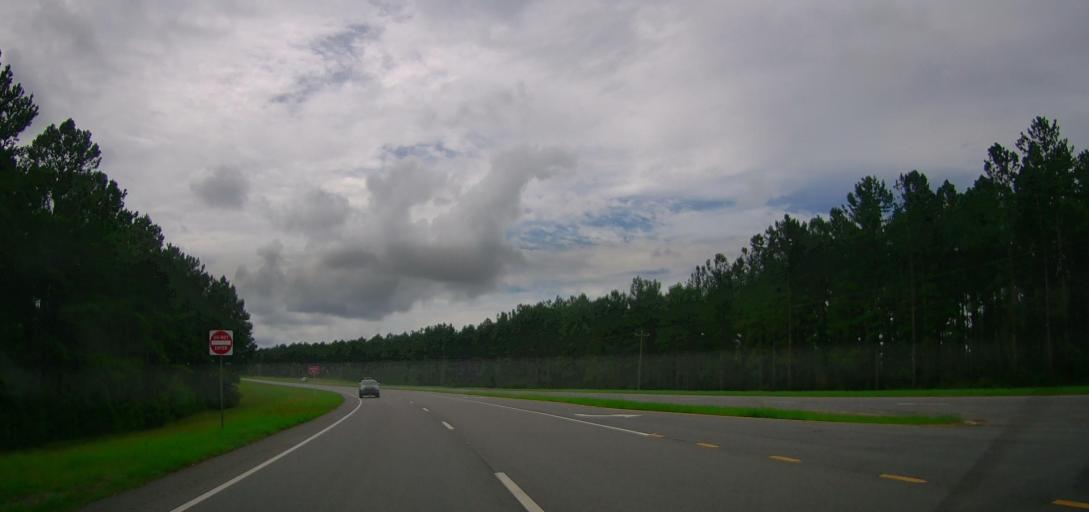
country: US
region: Georgia
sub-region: Telfair County
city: Lumber City
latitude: 31.9895
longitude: -82.7489
